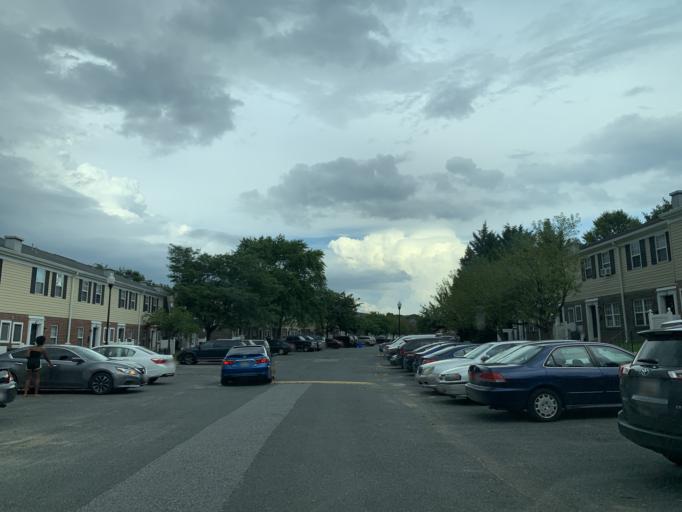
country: US
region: Maryland
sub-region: Baltimore County
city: Essex
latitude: 39.2994
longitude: -76.4551
